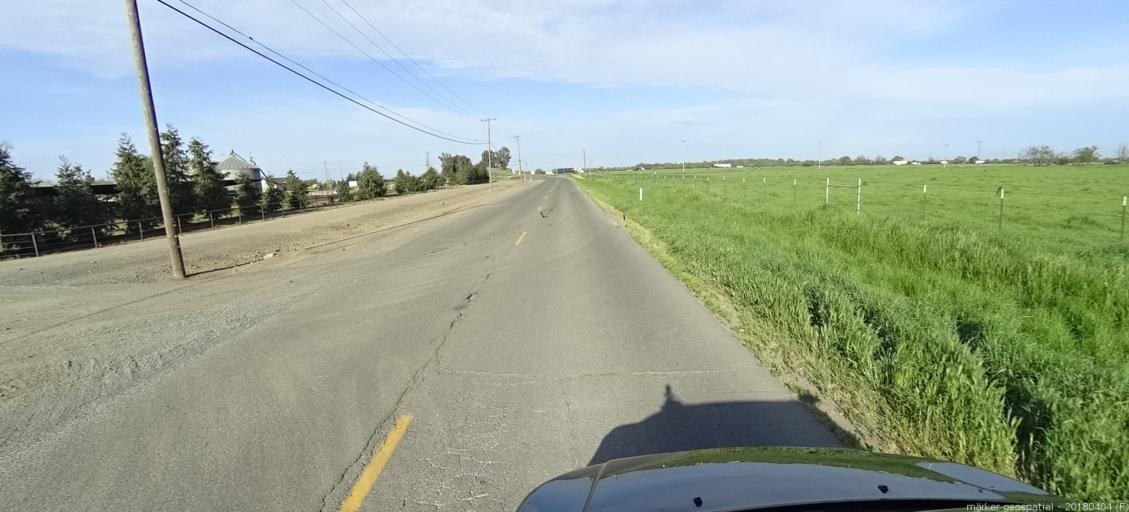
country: US
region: California
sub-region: Sacramento County
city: Galt
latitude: 38.3257
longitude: -121.3229
